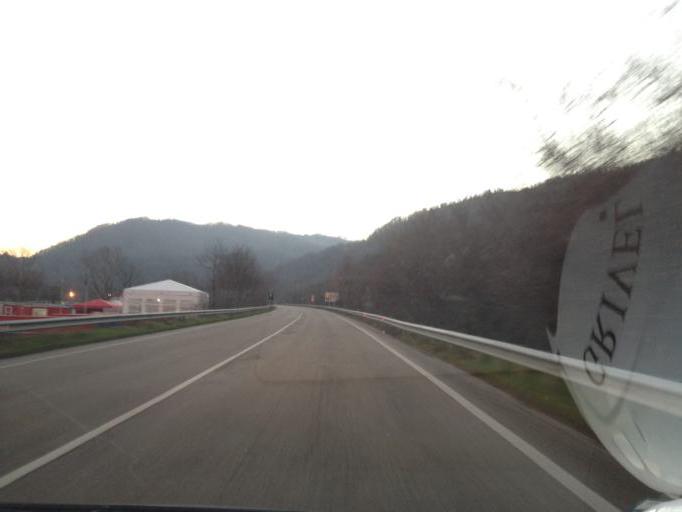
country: IT
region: The Marches
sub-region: Provincia di Ascoli Piceno
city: Arquata del Tronto
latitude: 42.7443
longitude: 13.2669
